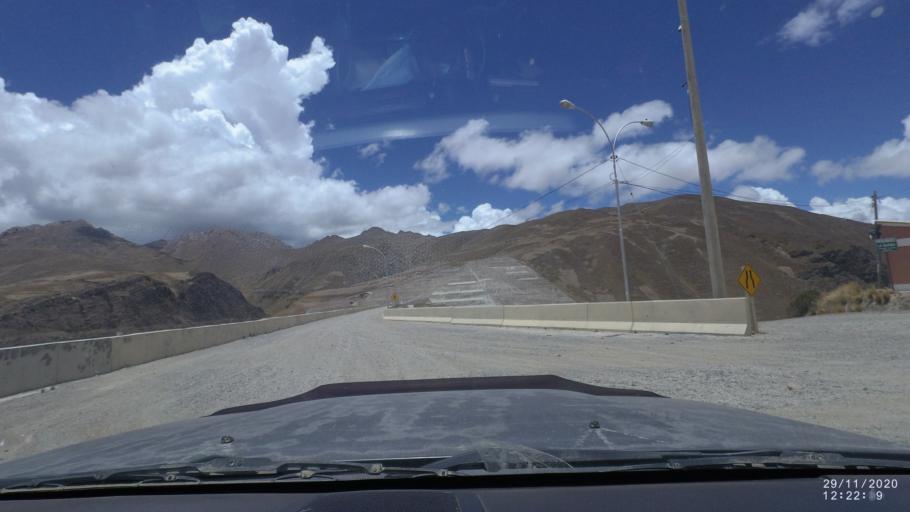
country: BO
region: Cochabamba
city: Cochabamba
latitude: -17.0963
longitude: -66.3282
